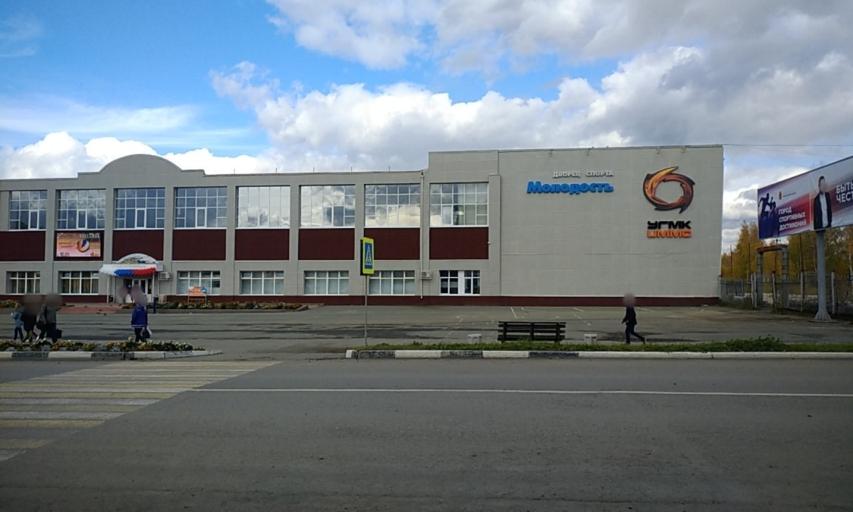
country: RU
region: Sverdlovsk
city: Krasnoural'sk
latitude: 58.3550
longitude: 60.0468
